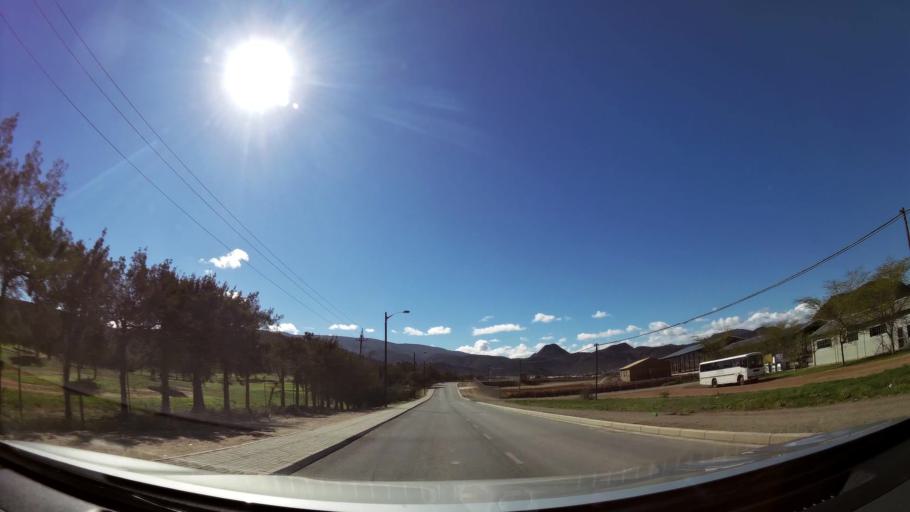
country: ZA
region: Western Cape
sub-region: Cape Winelands District Municipality
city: Ashton
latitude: -33.7740
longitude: 20.1347
